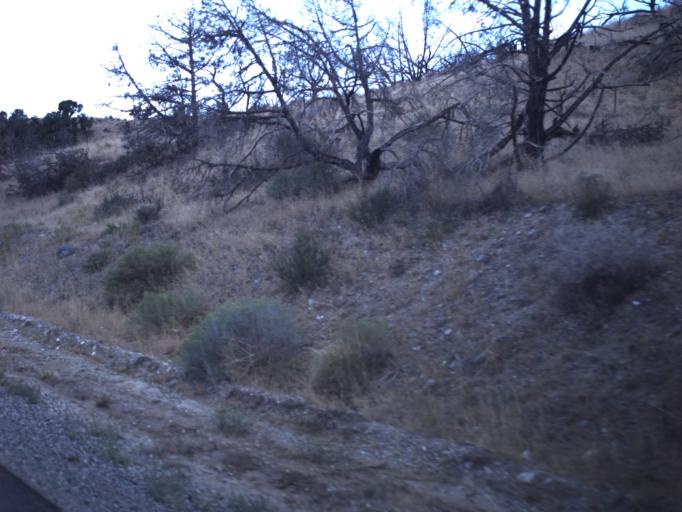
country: US
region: Utah
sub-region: Tooele County
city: Grantsville
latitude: 40.3309
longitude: -112.6188
